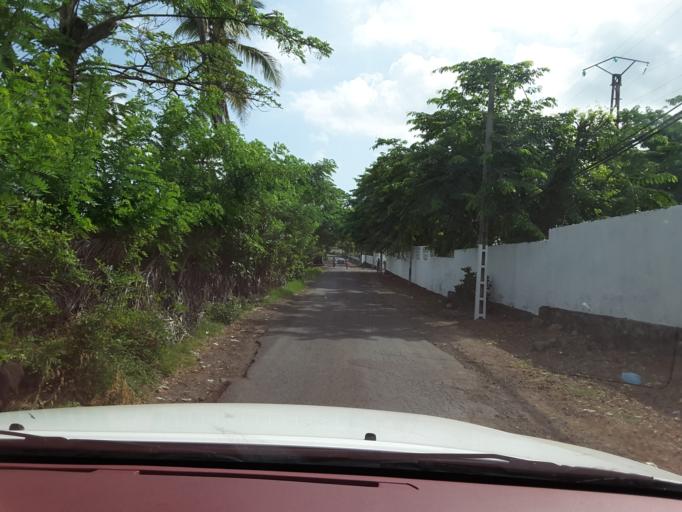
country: KM
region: Grande Comore
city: Mitsamiouli
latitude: -11.3936
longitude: 43.2858
